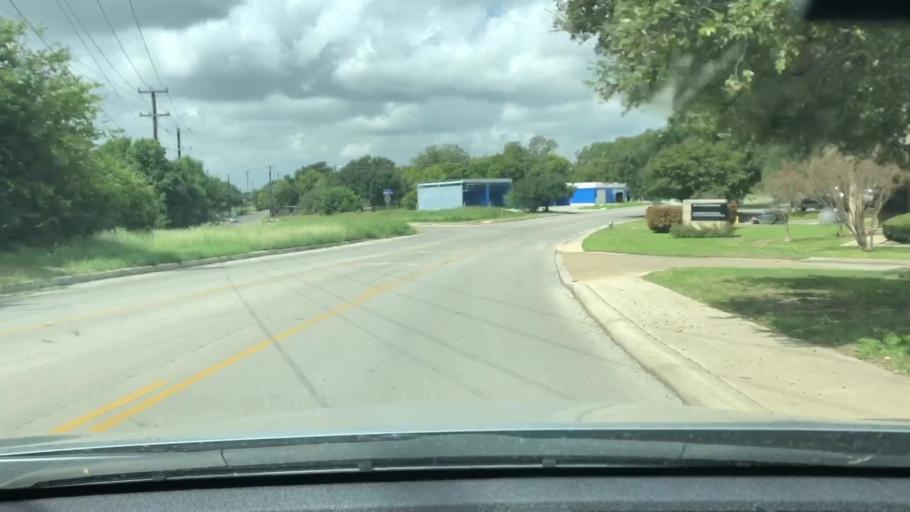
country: US
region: Texas
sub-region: Bexar County
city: Windcrest
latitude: 29.5315
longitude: -98.3771
